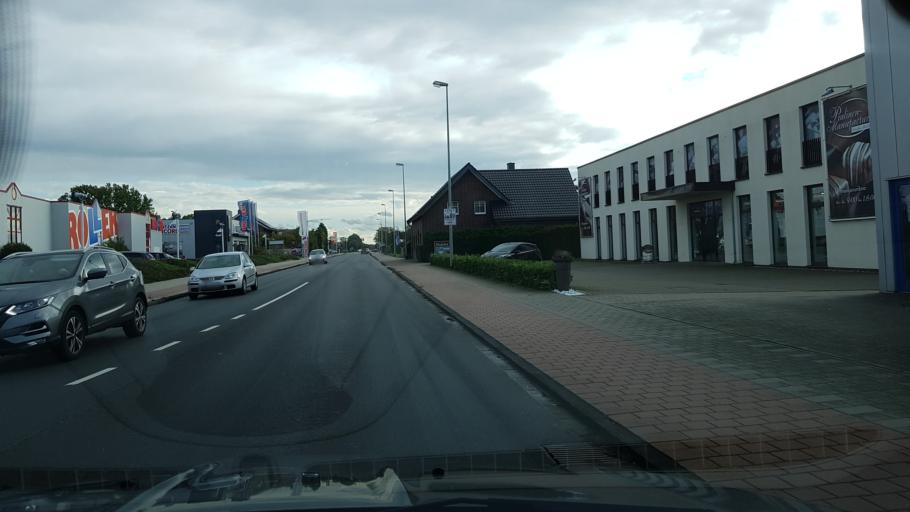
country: DE
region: North Rhine-Westphalia
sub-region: Regierungsbezirk Munster
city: Rhede
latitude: 51.8331
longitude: 6.7065
